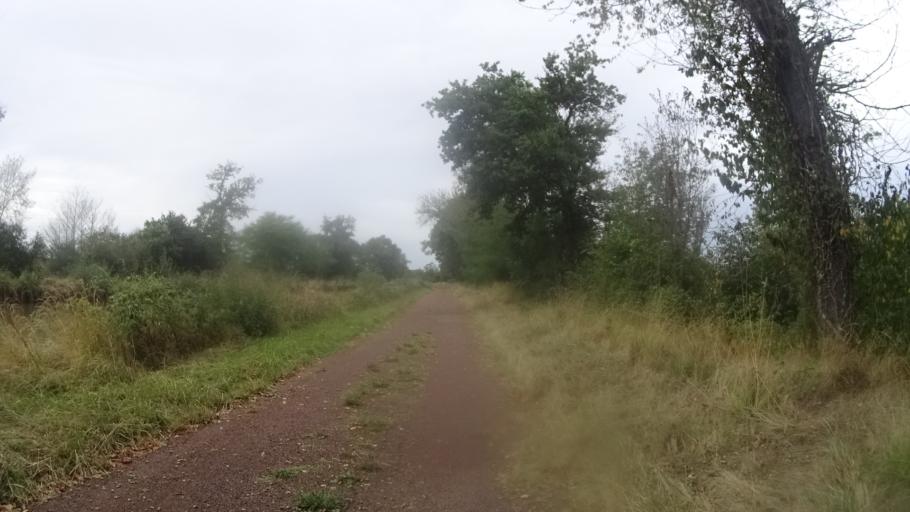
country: FR
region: Bourgogne
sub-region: Departement de la Nievre
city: Imphy
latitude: 46.8547
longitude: 3.2947
